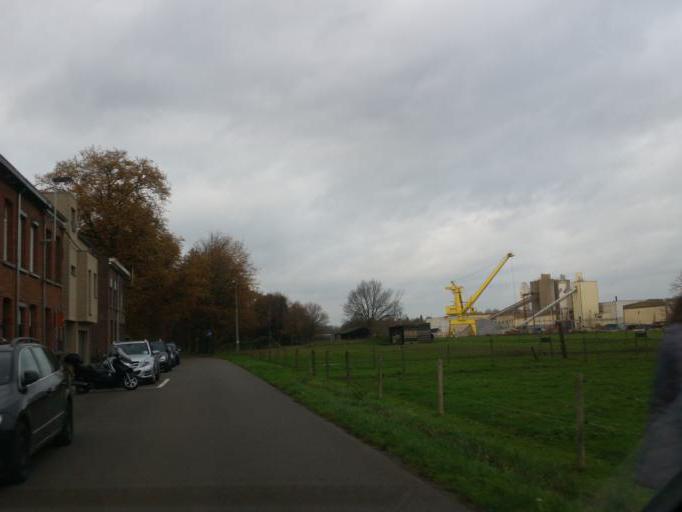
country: BE
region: Flanders
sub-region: Provincie Antwerpen
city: Lier
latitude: 51.1360
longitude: 4.5876
